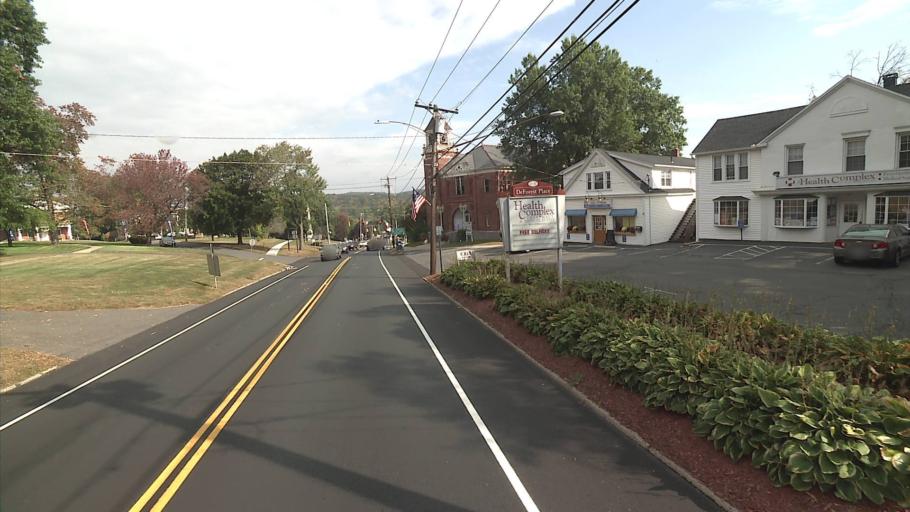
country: US
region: Connecticut
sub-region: Litchfield County
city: Watertown
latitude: 41.6049
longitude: -73.1193
